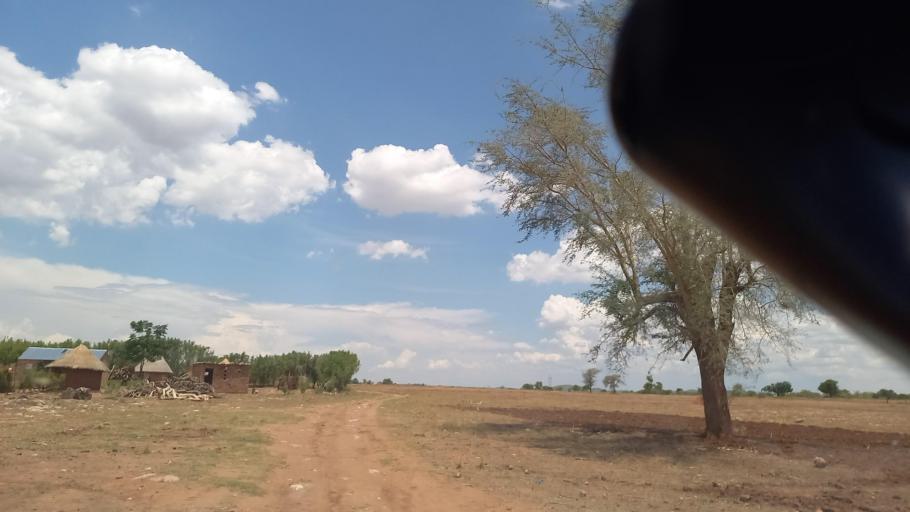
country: ZM
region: Southern
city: Mazabuka
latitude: -16.1100
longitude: 27.8248
